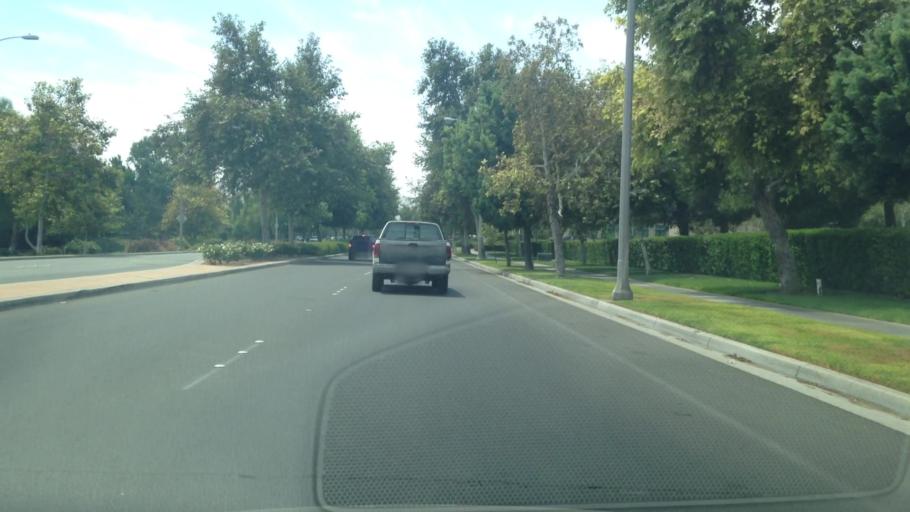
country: US
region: California
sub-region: Riverside County
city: Home Gardens
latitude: 33.9035
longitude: -117.4939
